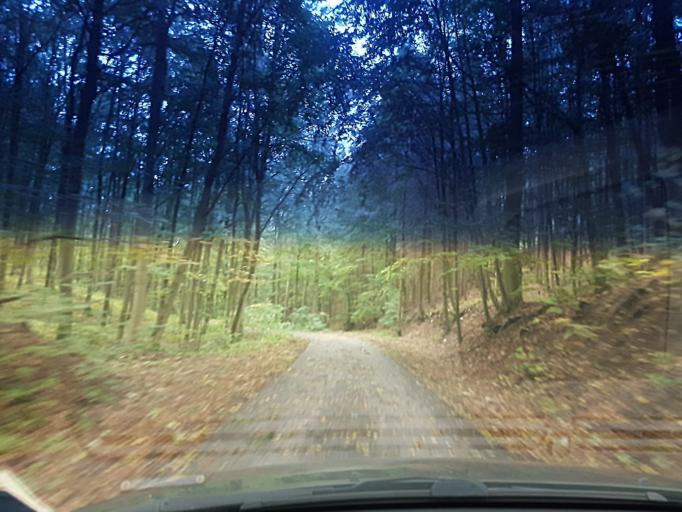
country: DE
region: Bavaria
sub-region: Upper Franconia
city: Schesslitz
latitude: 49.9887
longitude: 11.0838
